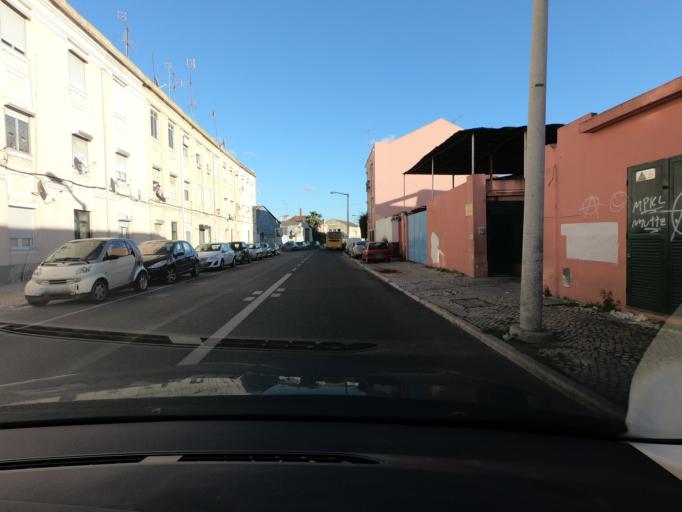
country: PT
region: Lisbon
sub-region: Lisbon
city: Lisbon
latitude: 38.7294
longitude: -9.1155
